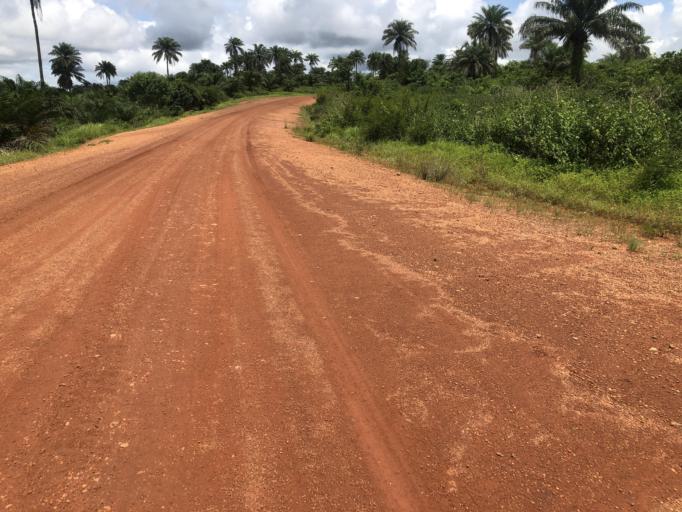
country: SL
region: Northern Province
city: Port Loko
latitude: 8.7137
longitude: -12.8288
